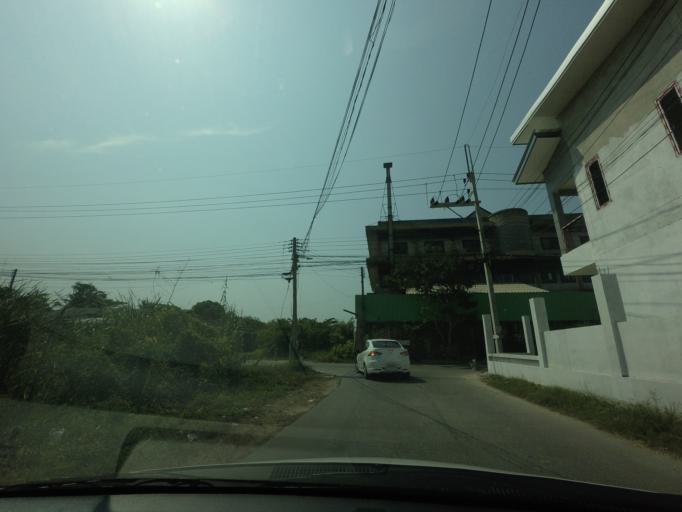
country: TH
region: Nakhon Pathom
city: Sam Phran
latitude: 13.7265
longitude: 100.2666
